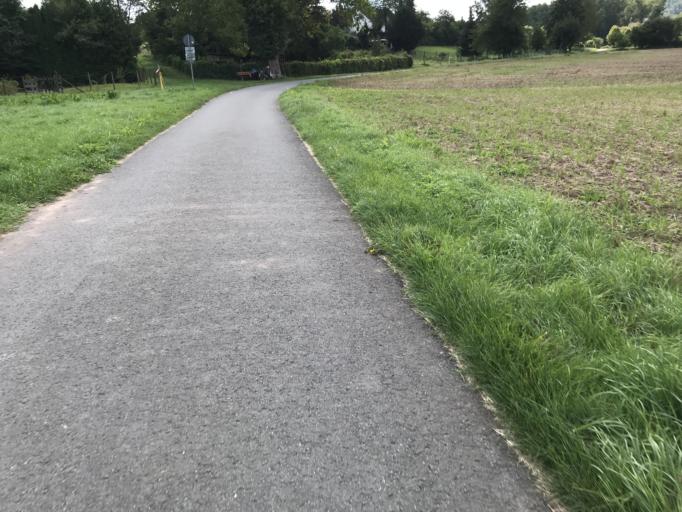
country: DE
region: Hesse
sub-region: Regierungsbezirk Kassel
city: Bad Sooden-Allendorf
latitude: 51.2794
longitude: 9.9676
